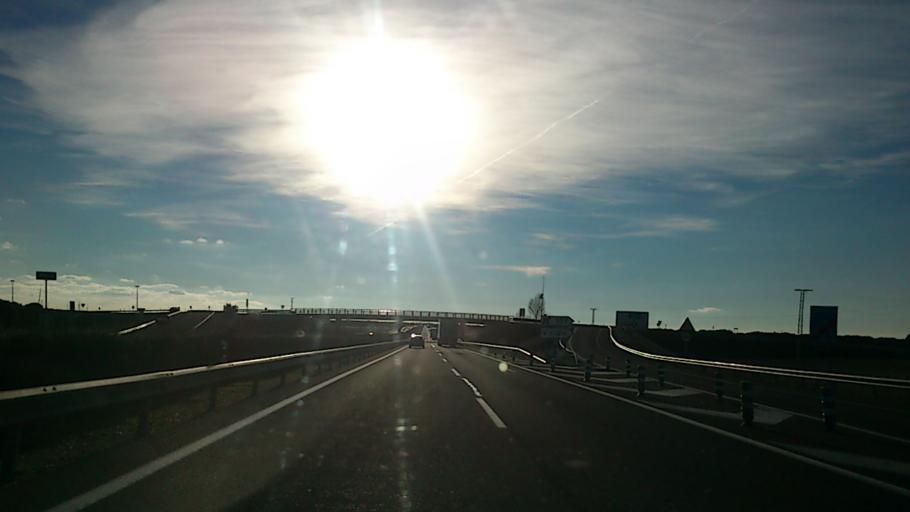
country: ES
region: Castille-La Mancha
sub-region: Provincia de Guadalajara
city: Mirabueno
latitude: 40.9317
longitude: -2.7121
